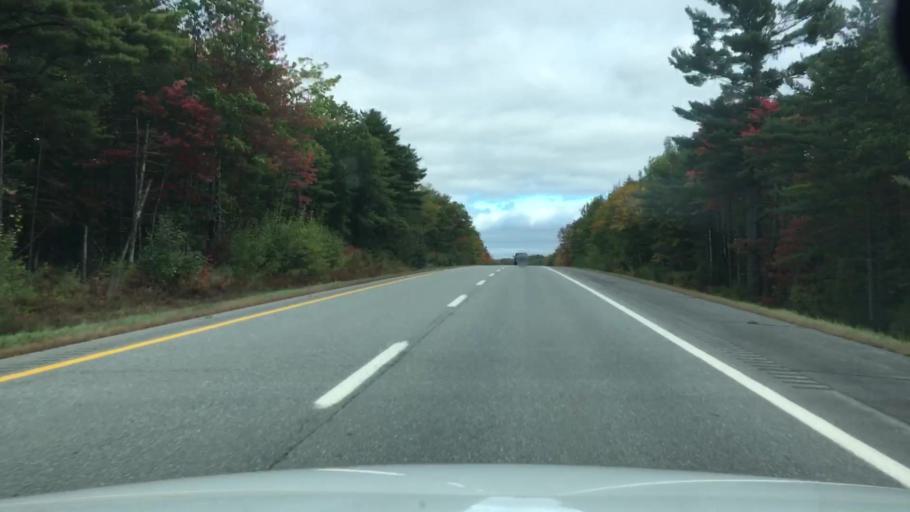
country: US
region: Maine
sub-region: Penobscot County
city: Carmel
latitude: 44.7780
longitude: -69.0607
